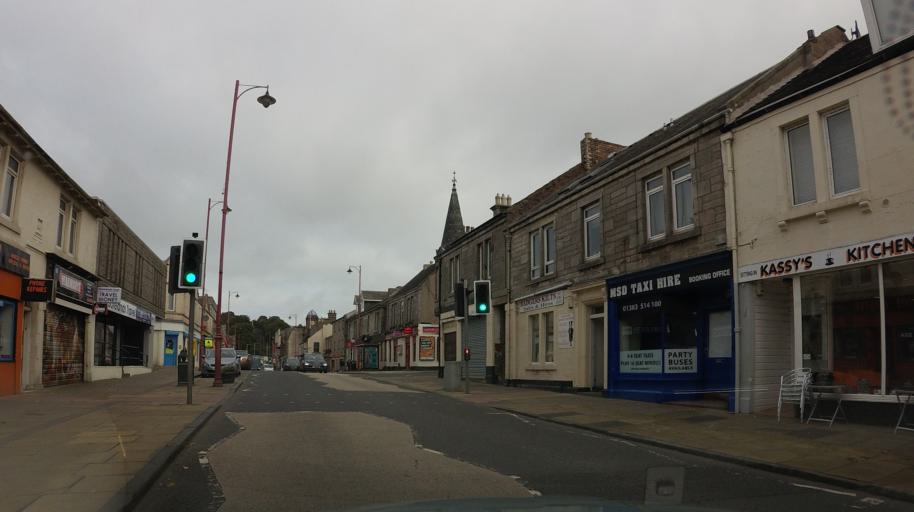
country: GB
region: Scotland
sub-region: Fife
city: Cowdenbeath
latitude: 56.1120
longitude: -3.3441
